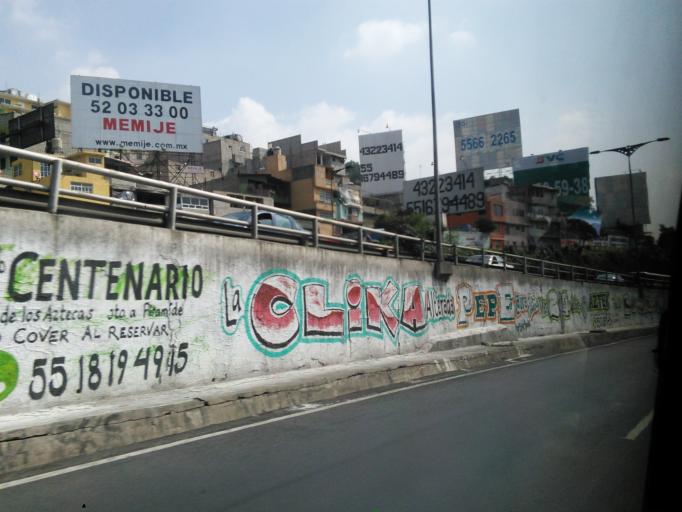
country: MX
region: Mexico City
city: Gustavo A. Madero
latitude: 19.5101
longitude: -99.1060
